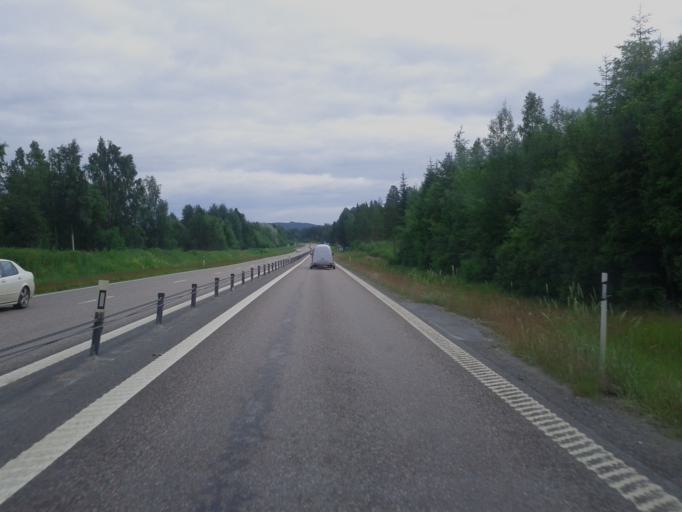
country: SE
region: Vaesternorrland
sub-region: OErnskoeldsviks Kommun
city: Ornskoldsvik
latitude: 63.2871
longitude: 18.5933
